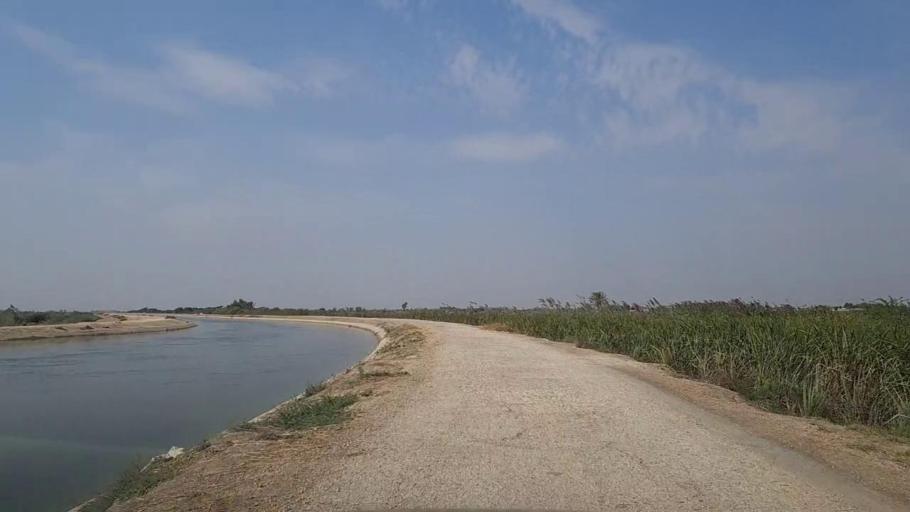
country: PK
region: Sindh
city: Thatta
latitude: 24.7494
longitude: 67.7709
